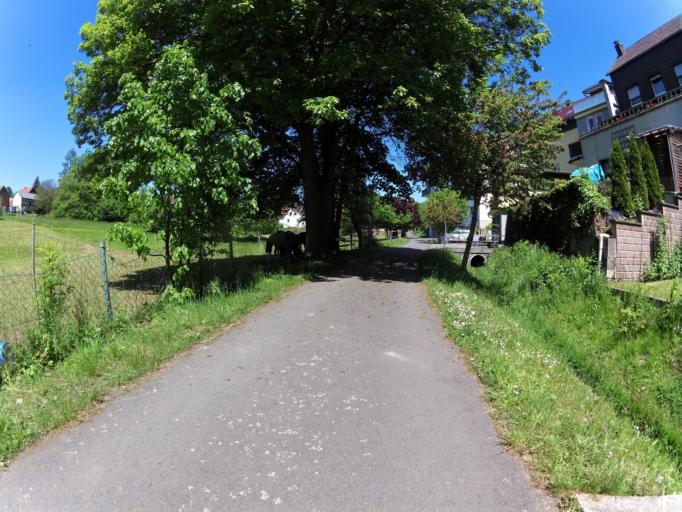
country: DE
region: Thuringia
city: Dankmarshausen
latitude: 50.9499
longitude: 9.9930
